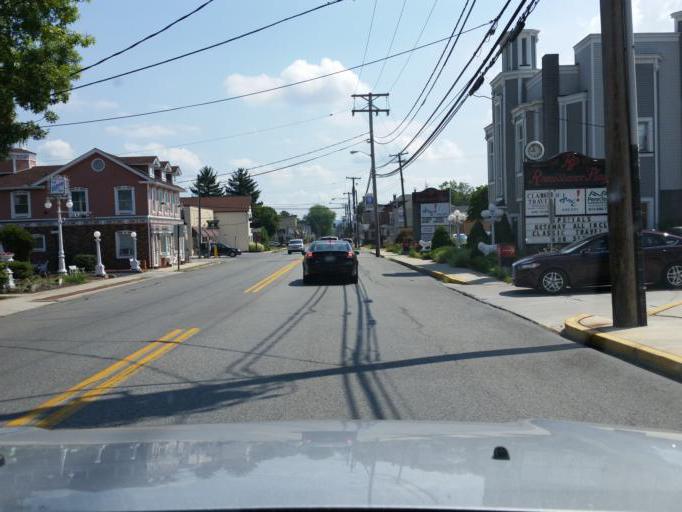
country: US
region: Pennsylvania
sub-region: Blair County
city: Duncansville
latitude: 40.4225
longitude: -78.4367
